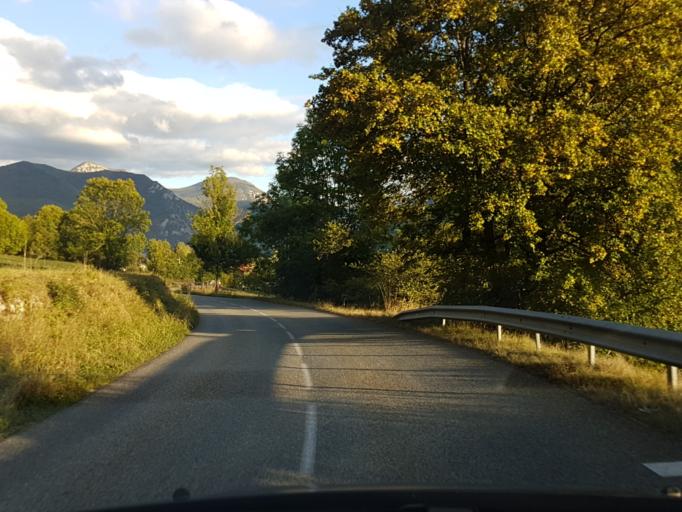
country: FR
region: Midi-Pyrenees
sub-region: Departement de l'Ariege
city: Tarascon-sur-Ariege
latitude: 42.8621
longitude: 1.5726
